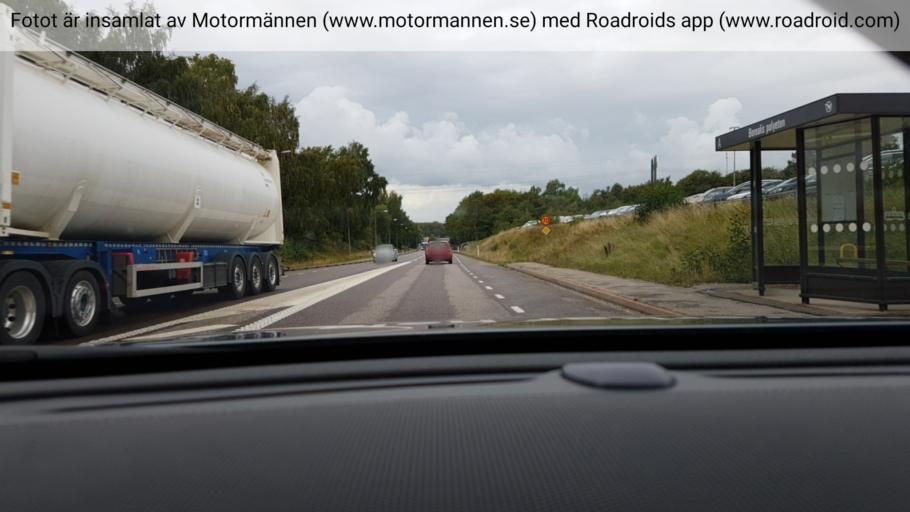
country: SE
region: Vaestra Goetaland
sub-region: Stenungsunds Kommun
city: Stenungsund
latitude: 58.0755
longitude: 11.8397
